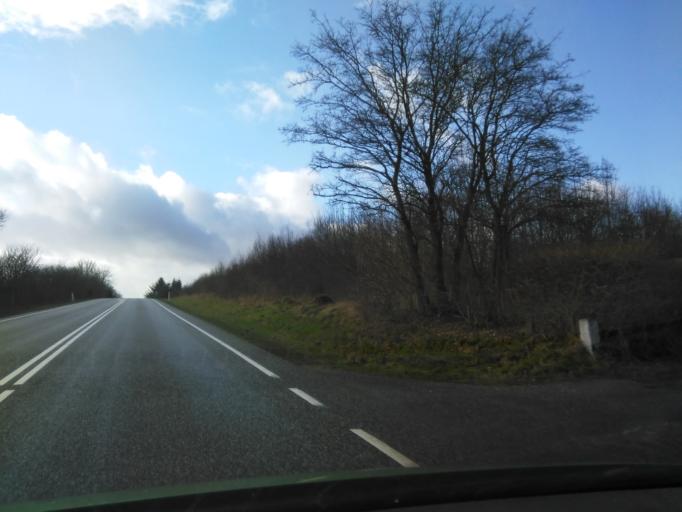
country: DK
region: Central Jutland
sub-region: Skanderborg Kommune
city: Skanderborg
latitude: 56.0228
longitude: 9.8952
